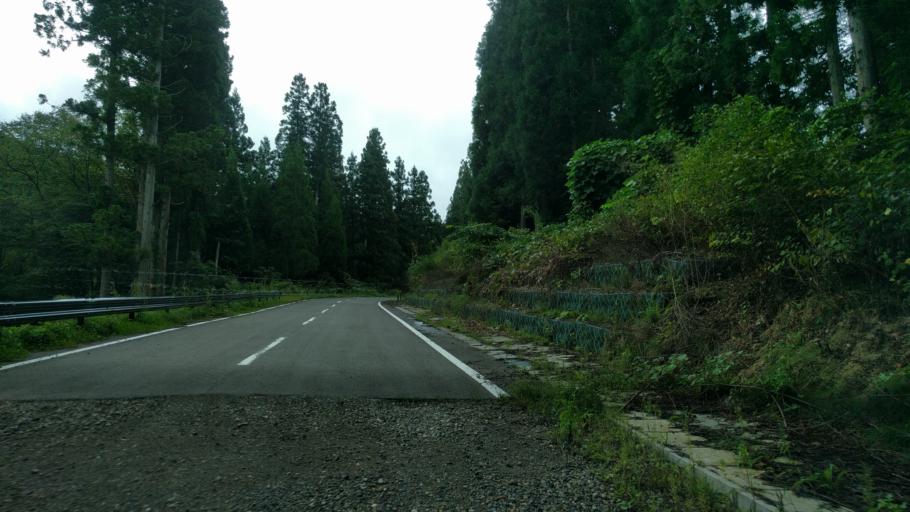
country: JP
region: Fukushima
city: Kitakata
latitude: 37.5210
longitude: 139.7601
